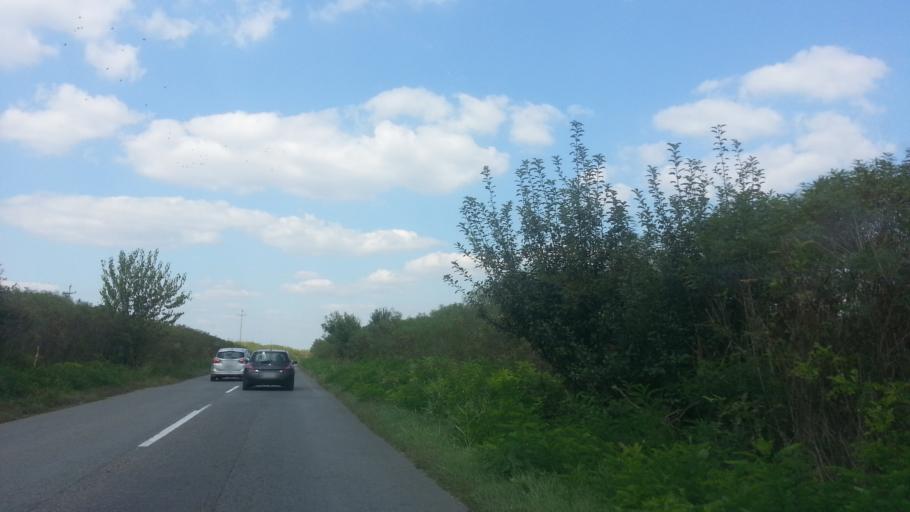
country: RS
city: Novi Banovci
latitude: 44.9265
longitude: 20.2801
